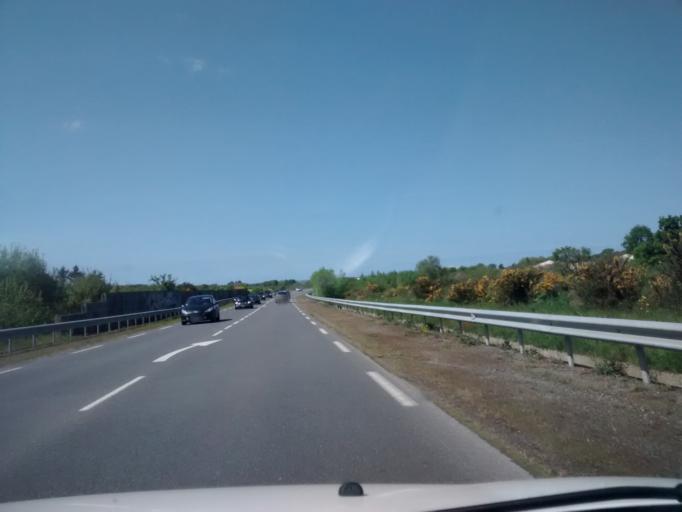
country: FR
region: Brittany
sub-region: Departement d'Ille-et-Vilaine
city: Pleurtuit
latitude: 48.5734
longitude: -2.0716
